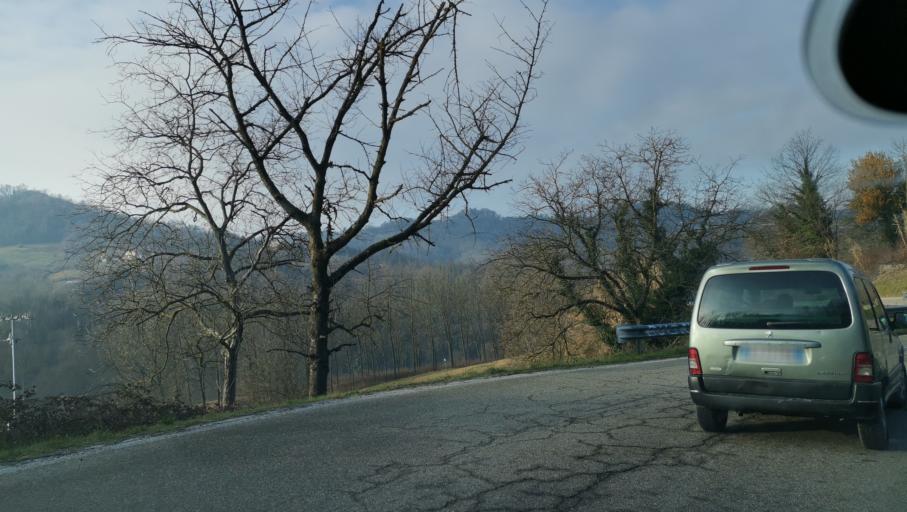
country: IT
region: Piedmont
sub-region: Provincia di Asti
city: Berzano di San Pietro
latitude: 45.0997
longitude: 7.9458
